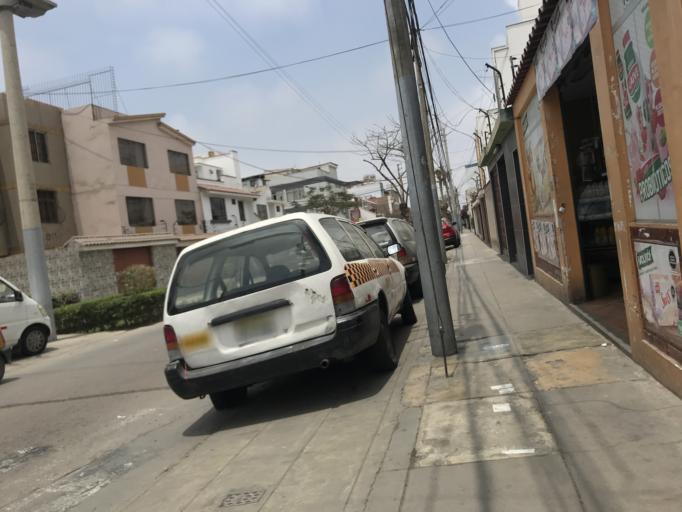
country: PE
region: Lima
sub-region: Lima
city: San Isidro
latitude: -12.0816
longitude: -77.0763
